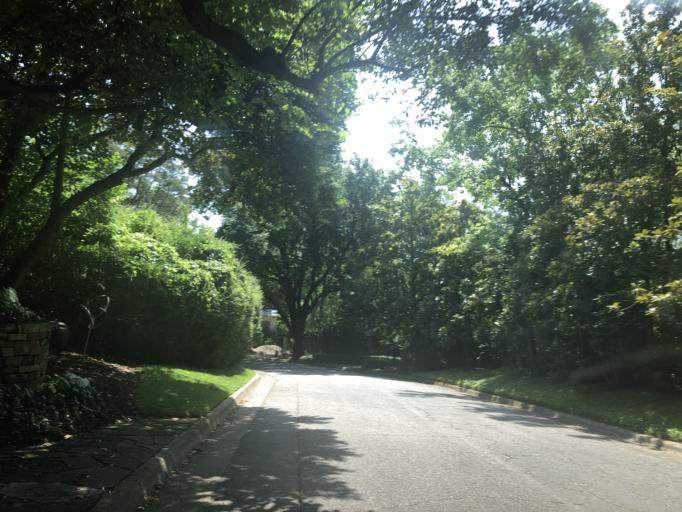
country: US
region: Texas
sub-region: Dallas County
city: University Park
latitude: 32.8796
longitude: -96.8259
